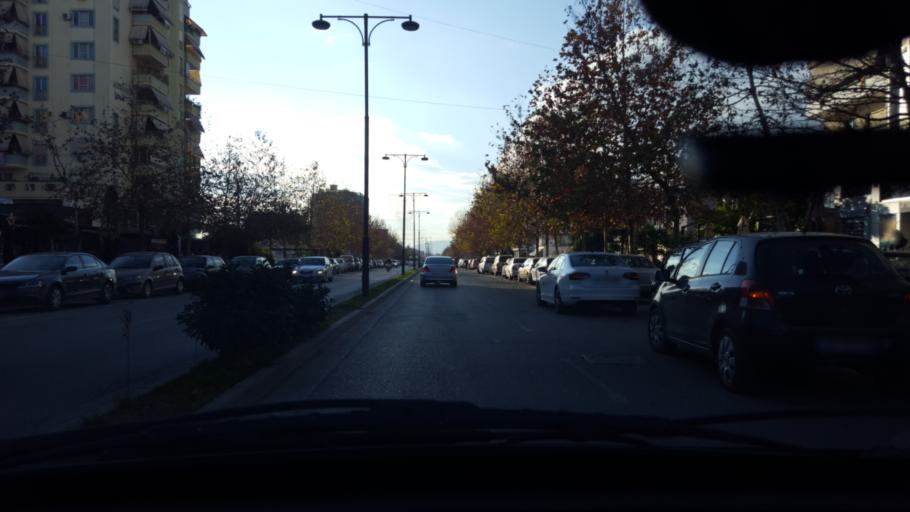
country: AL
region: Elbasan
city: Elbasan
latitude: 41.1103
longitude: 20.0784
